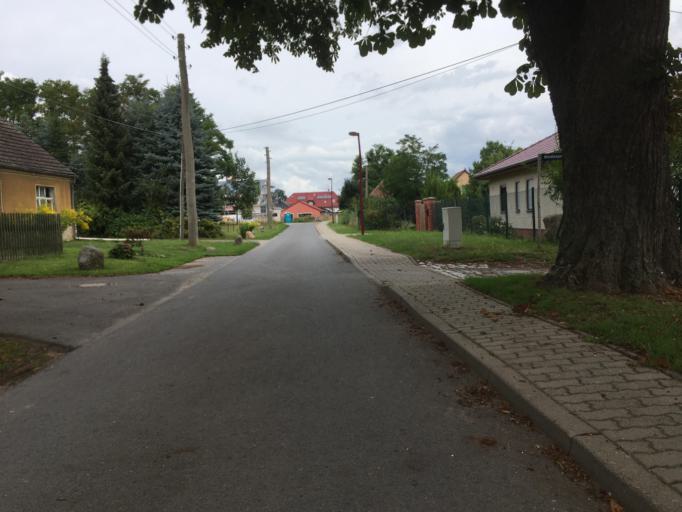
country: DE
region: Brandenburg
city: Prenzlau
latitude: 53.2784
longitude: 13.8441
